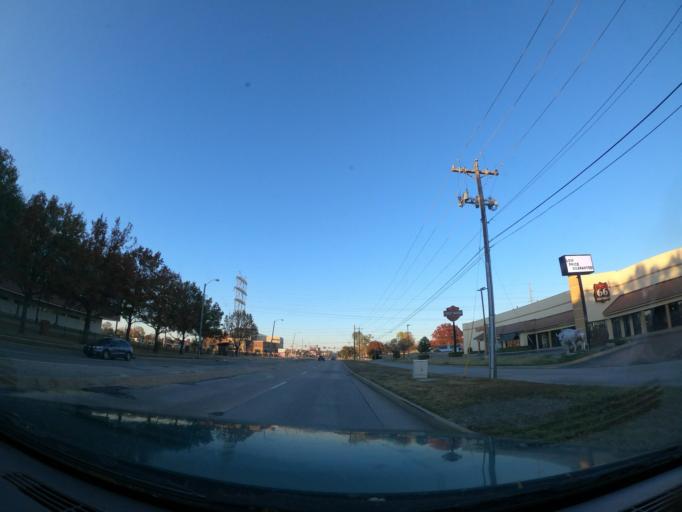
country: US
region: Oklahoma
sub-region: Tulsa County
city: Broken Arrow
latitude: 36.1107
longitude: -95.8865
